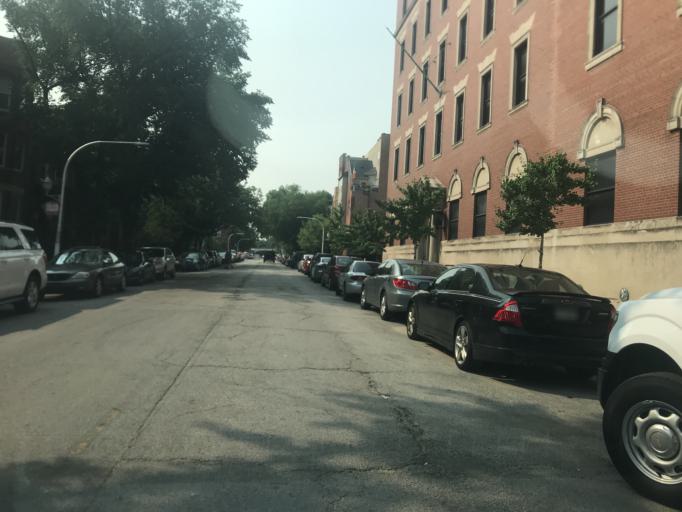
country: US
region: Illinois
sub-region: Cook County
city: Lincolnwood
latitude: 41.9467
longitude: -87.6542
